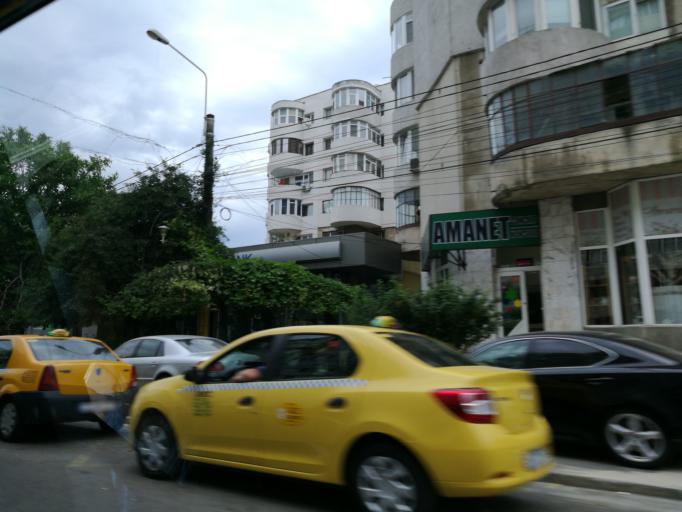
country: RO
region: Constanta
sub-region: Municipiul Constanta
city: Constanta
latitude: 44.1782
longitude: 28.6361
